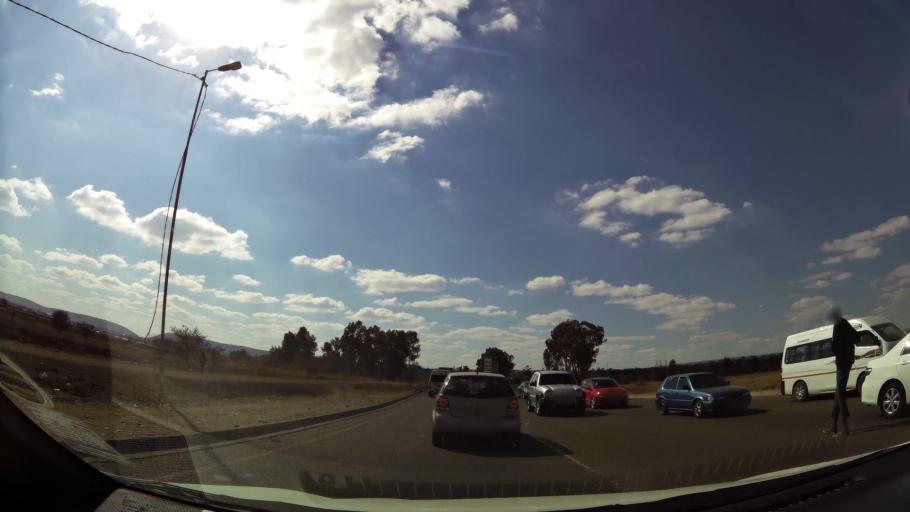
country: ZA
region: Gauteng
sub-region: City of Tshwane Metropolitan Municipality
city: Cullinan
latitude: -25.7507
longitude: 28.3690
